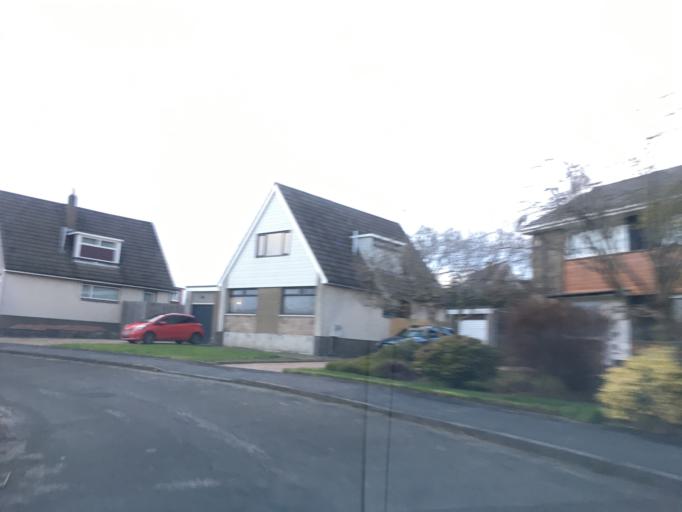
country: GB
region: Scotland
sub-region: Stirling
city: Stirling
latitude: 56.1063
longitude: -3.9484
